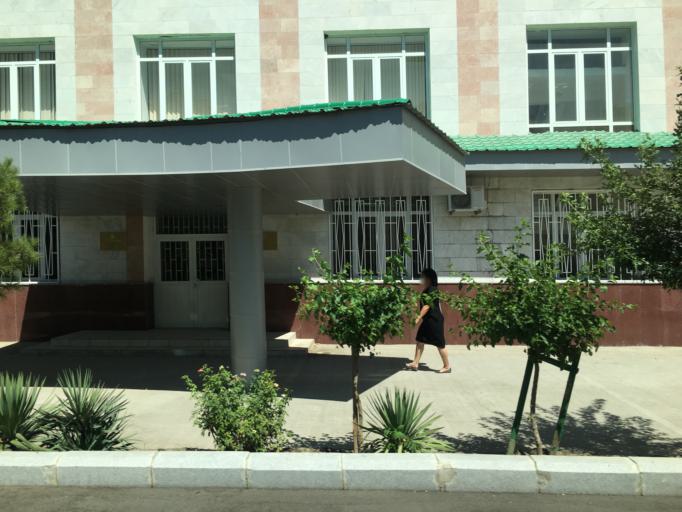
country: TM
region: Ahal
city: Ashgabat
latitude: 37.9413
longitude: 58.3751
